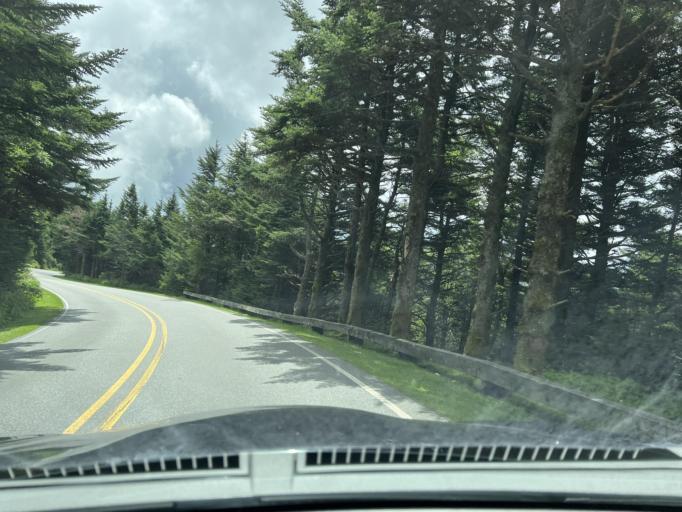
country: US
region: North Carolina
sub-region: Yancey County
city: Burnsville
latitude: 35.7663
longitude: -82.2666
